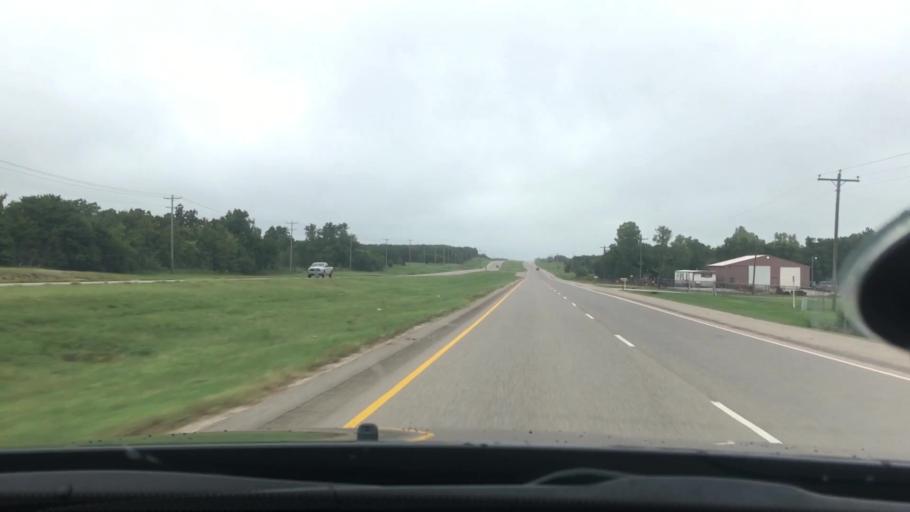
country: US
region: Oklahoma
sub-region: Seminole County
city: Seminole
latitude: 35.3224
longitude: -96.6713
